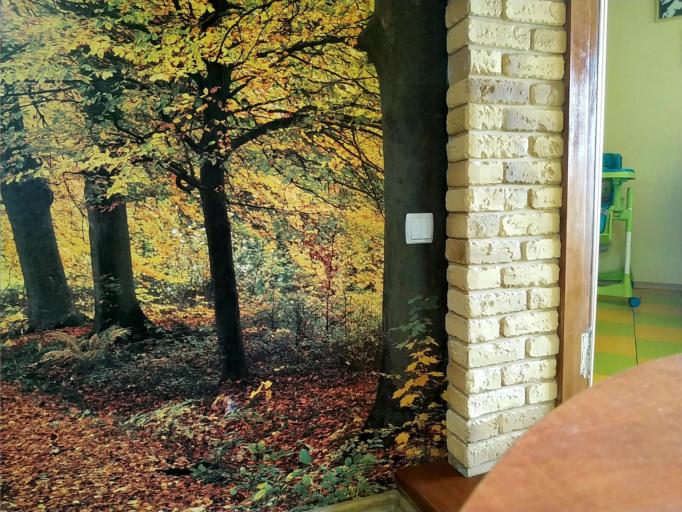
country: RU
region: Smolensk
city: Ozernyy
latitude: 55.4358
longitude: 32.6968
